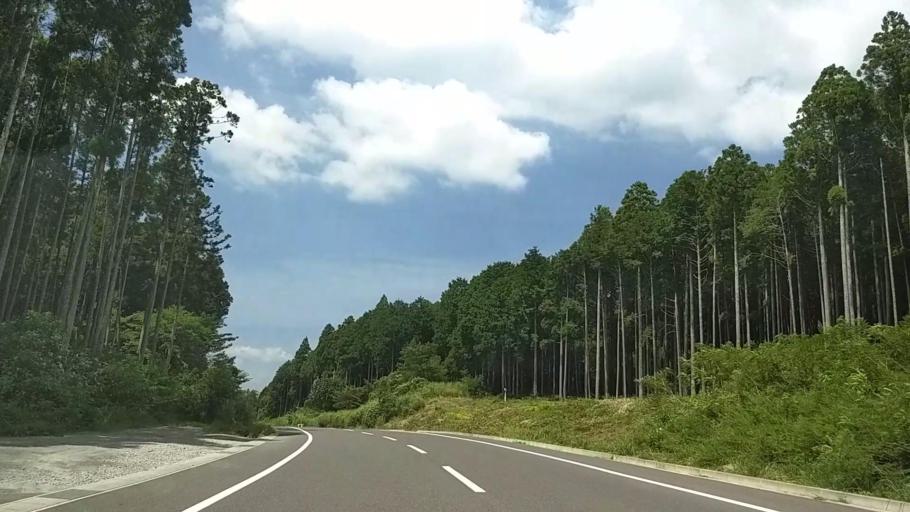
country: JP
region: Shizuoka
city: Fujinomiya
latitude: 35.2552
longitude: 138.6818
